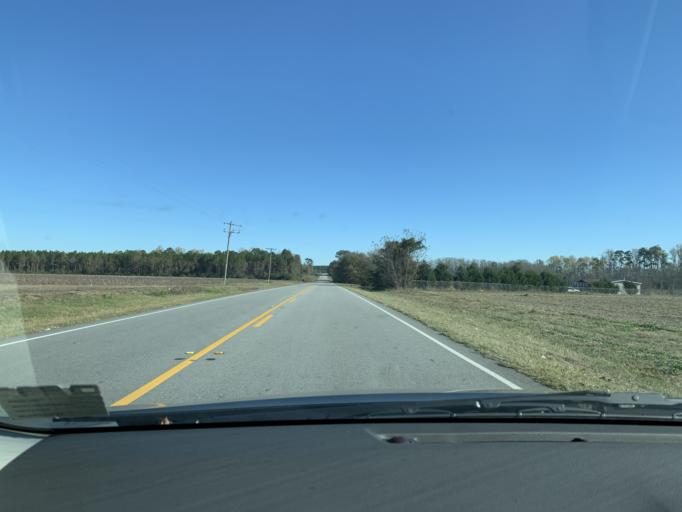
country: US
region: Georgia
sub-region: Ben Hill County
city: Fitzgerald
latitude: 31.7164
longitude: -83.1880
